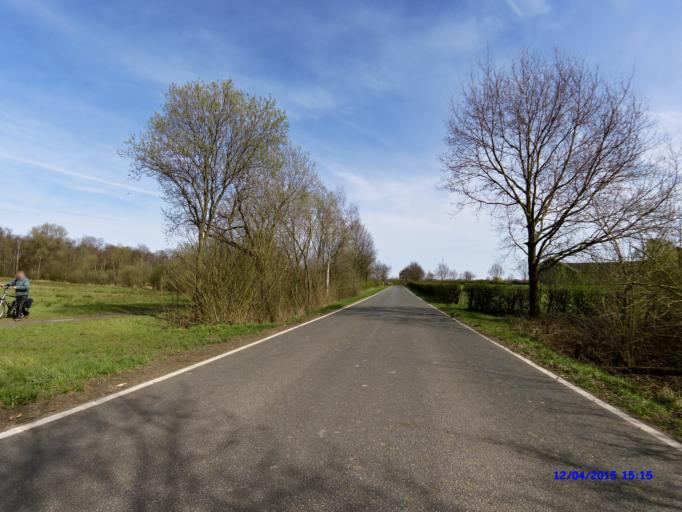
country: DE
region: North Rhine-Westphalia
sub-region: Regierungsbezirk Koln
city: Gangelt
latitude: 50.9562
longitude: 6.0203
